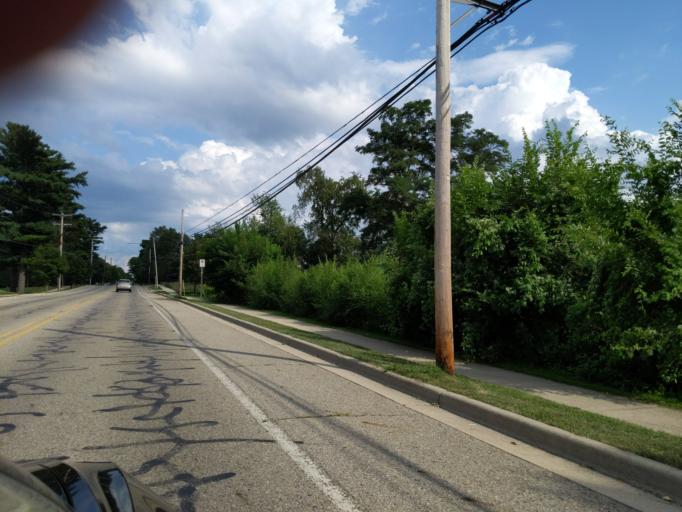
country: US
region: Michigan
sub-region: Clinton County
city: DeWitt
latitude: 42.8368
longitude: -84.5651
